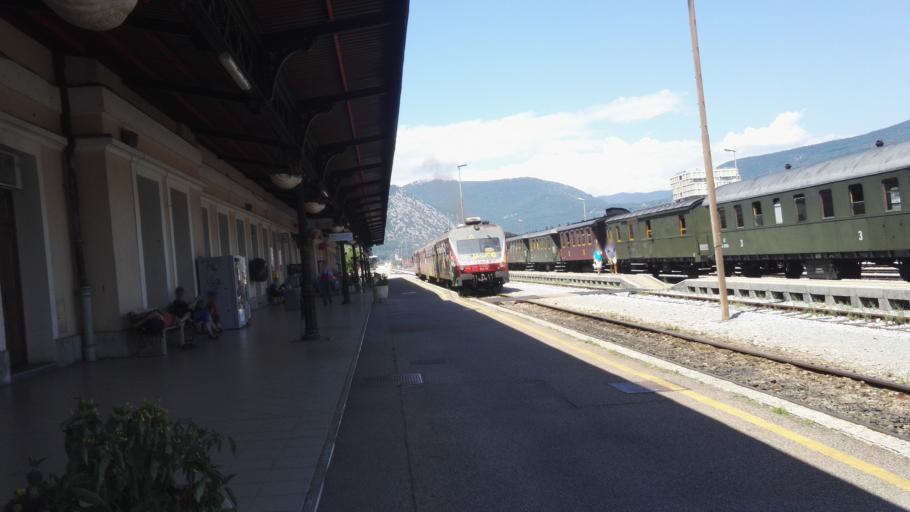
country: SI
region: Nova Gorica
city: Nova Gorica
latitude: 45.9548
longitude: 13.6353
